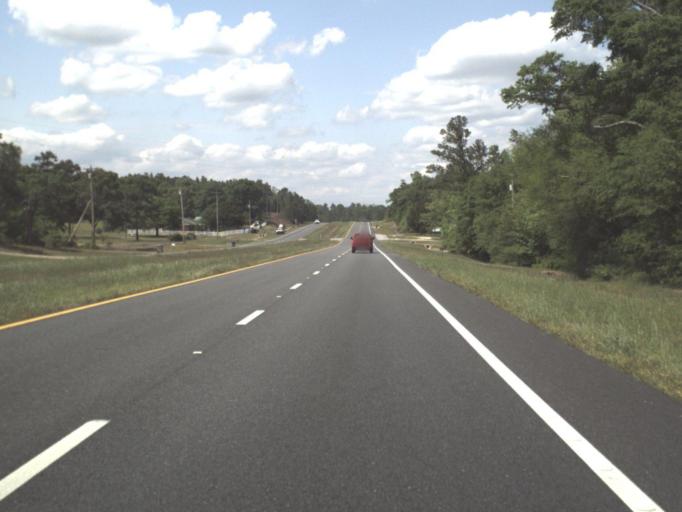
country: US
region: Florida
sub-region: Escambia County
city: Century
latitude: 30.8870
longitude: -87.3212
